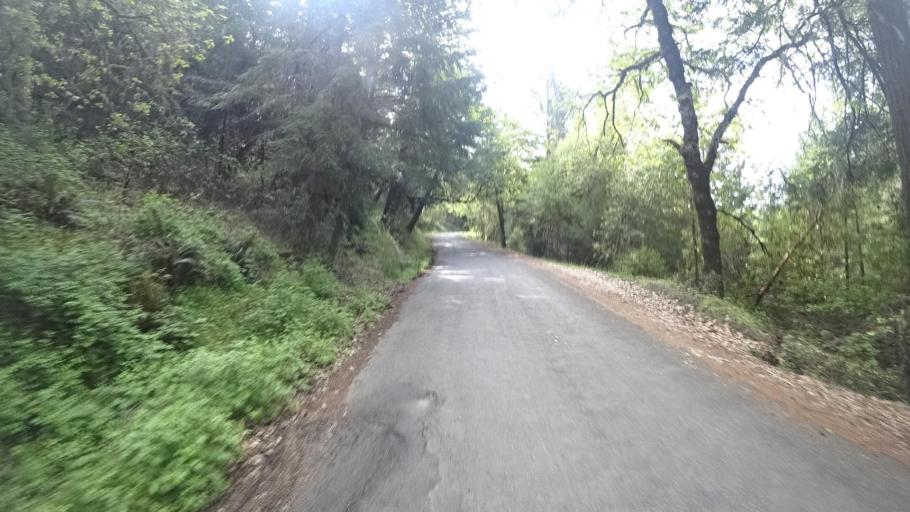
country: US
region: California
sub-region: Humboldt County
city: Redway
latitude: 40.1705
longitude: -123.5652
